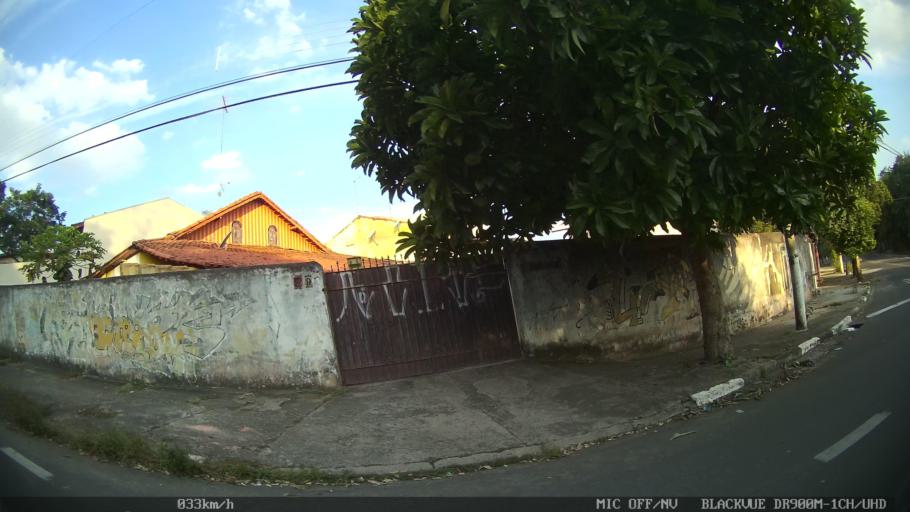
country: BR
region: Sao Paulo
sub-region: Hortolandia
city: Hortolandia
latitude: -22.8941
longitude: -47.1541
